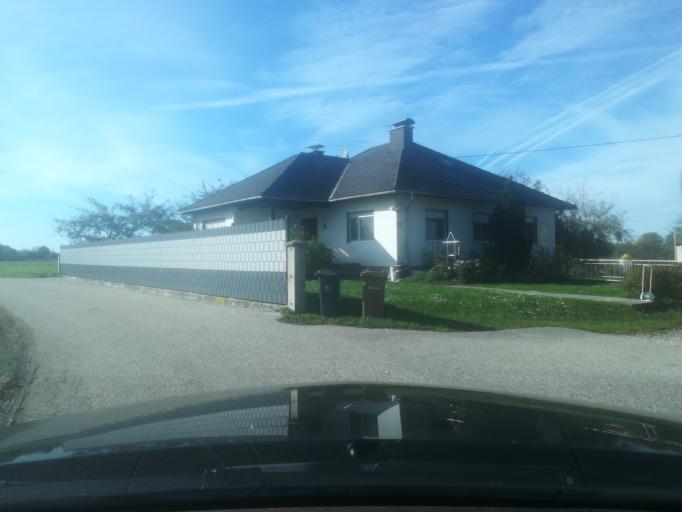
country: AT
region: Upper Austria
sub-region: Politischer Bezirk Linz-Land
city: Horsching
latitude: 48.2073
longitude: 14.1496
